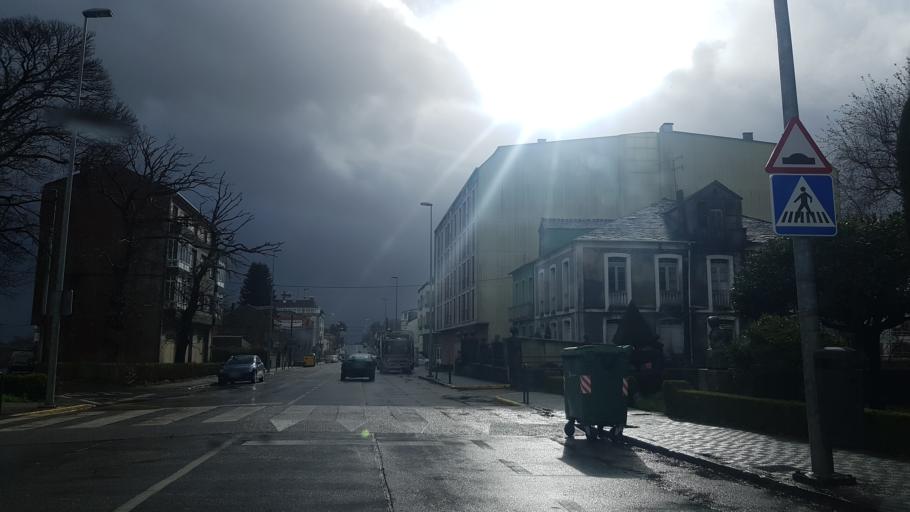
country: ES
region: Galicia
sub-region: Provincia de Lugo
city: Vilalba
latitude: 43.2914
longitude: -7.6795
